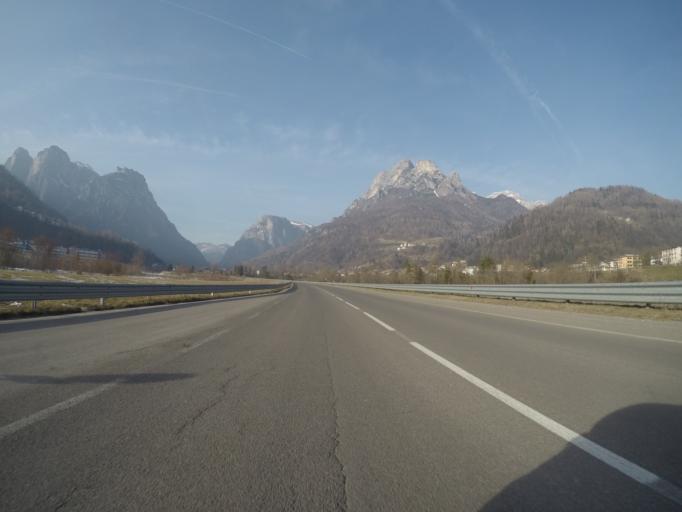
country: IT
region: Veneto
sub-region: Provincia di Belluno
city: Agordo
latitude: 46.2813
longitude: 12.0290
